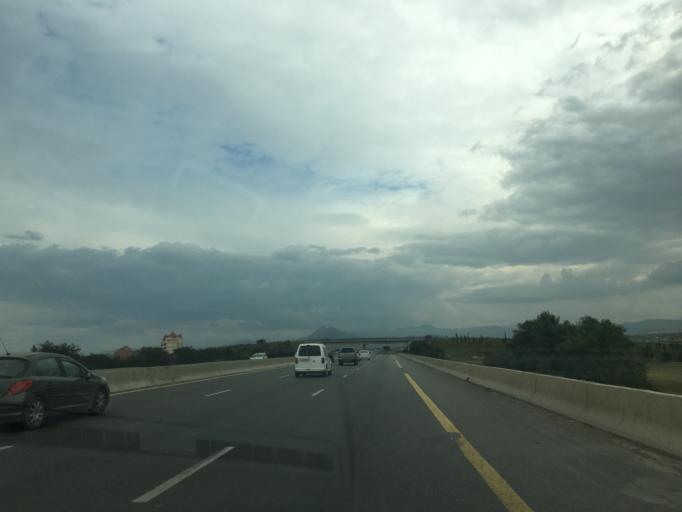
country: DZ
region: Bouira
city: Bouira
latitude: 36.3236
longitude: 3.9947
